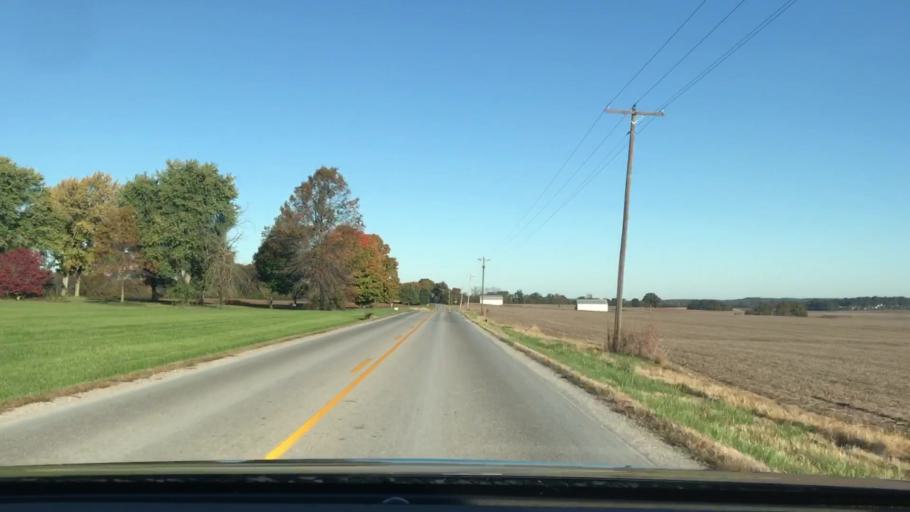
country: US
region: Kentucky
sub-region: Logan County
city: Auburn
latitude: 36.8400
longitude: -86.6927
